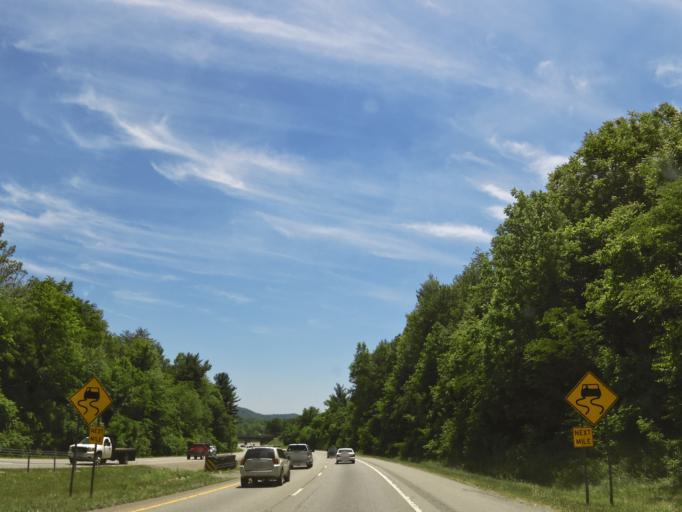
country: US
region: Tennessee
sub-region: Campbell County
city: Caryville
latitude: 36.2654
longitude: -84.1936
